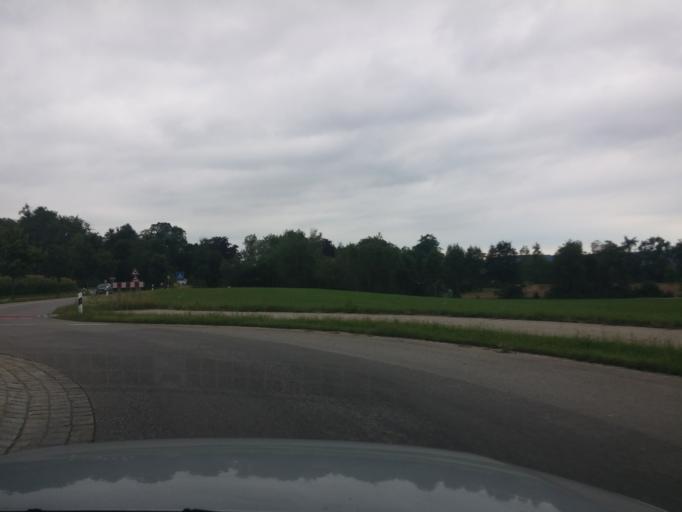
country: DE
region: Baden-Wuerttemberg
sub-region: Tuebingen Region
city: Aitrach
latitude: 47.9511
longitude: 10.1110
